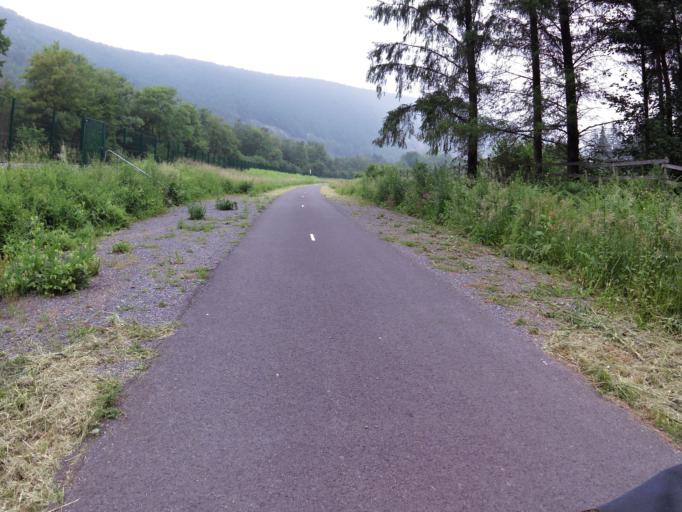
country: FR
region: Champagne-Ardenne
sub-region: Departement des Ardennes
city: Revin
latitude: 49.9754
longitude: 4.6633
